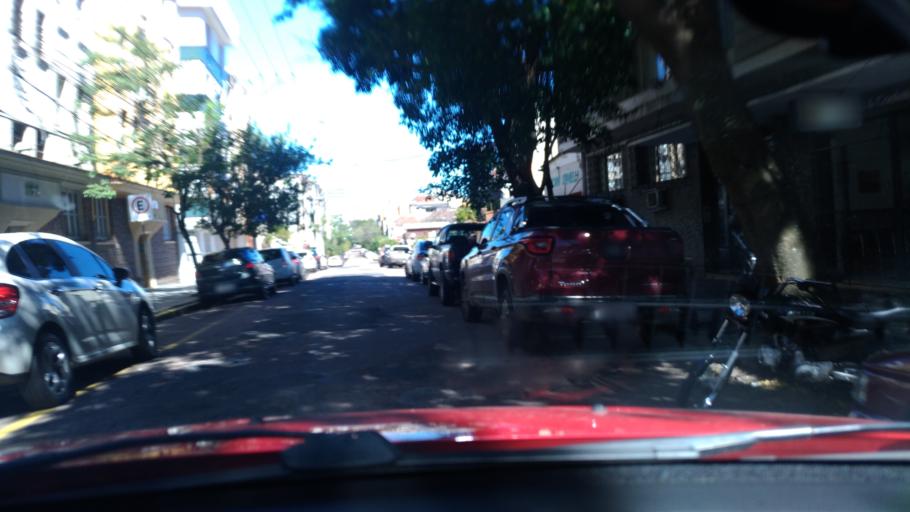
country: BR
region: Rio Grande do Sul
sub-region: Porto Alegre
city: Porto Alegre
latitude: -30.0395
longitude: -51.2093
